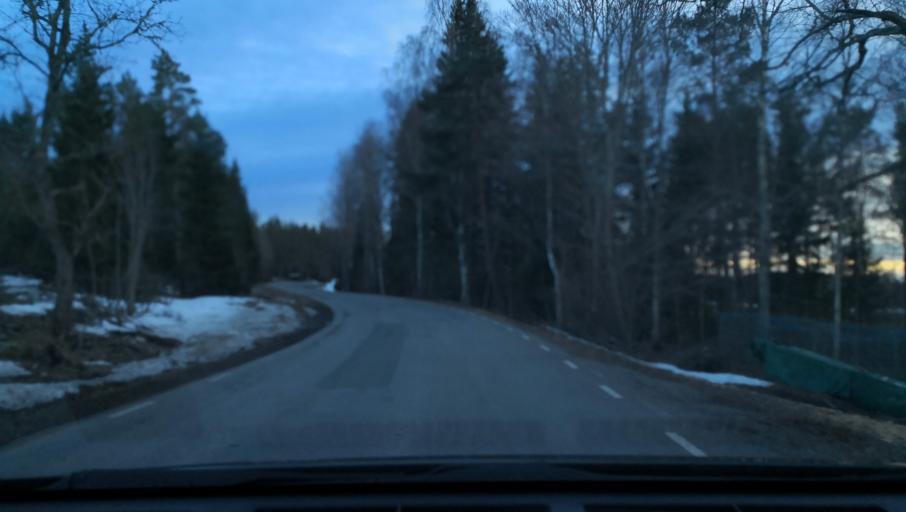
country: SE
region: Uppsala
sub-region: Osthammars Kommun
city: Osterbybruk
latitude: 60.2573
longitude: 17.9473
